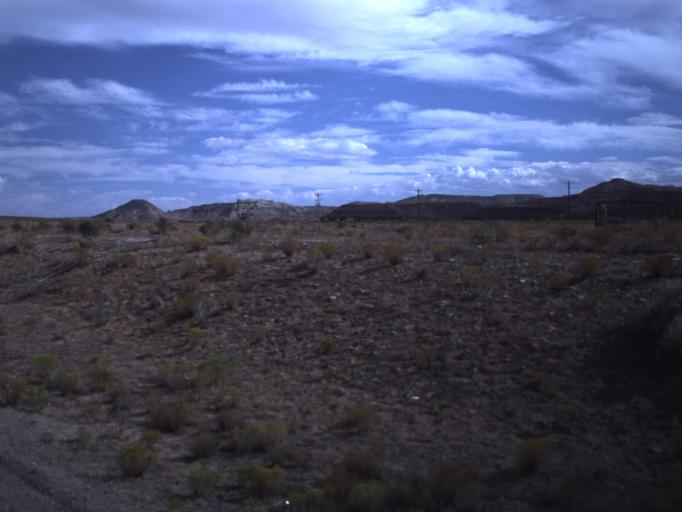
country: US
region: Utah
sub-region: San Juan County
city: Blanding
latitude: 37.2421
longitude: -109.2463
